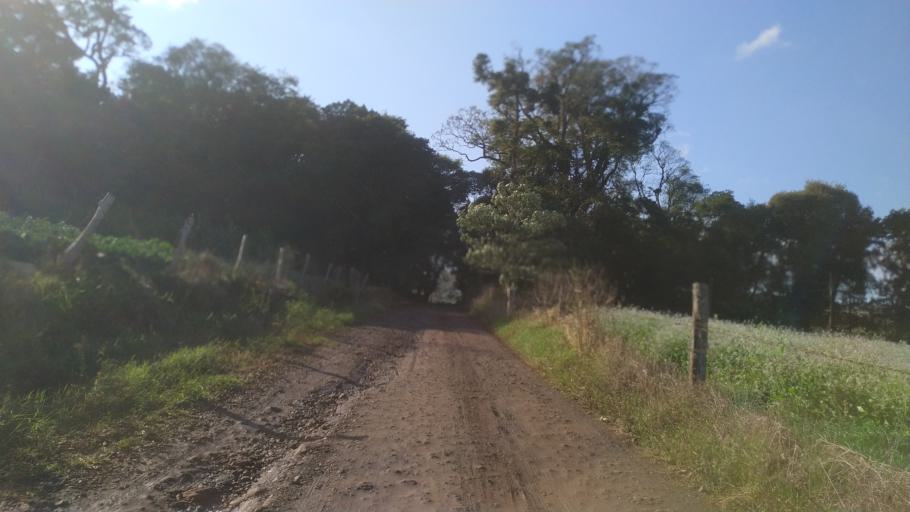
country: BR
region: Santa Catarina
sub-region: Chapeco
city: Chapeco
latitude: -27.0642
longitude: -52.6119
